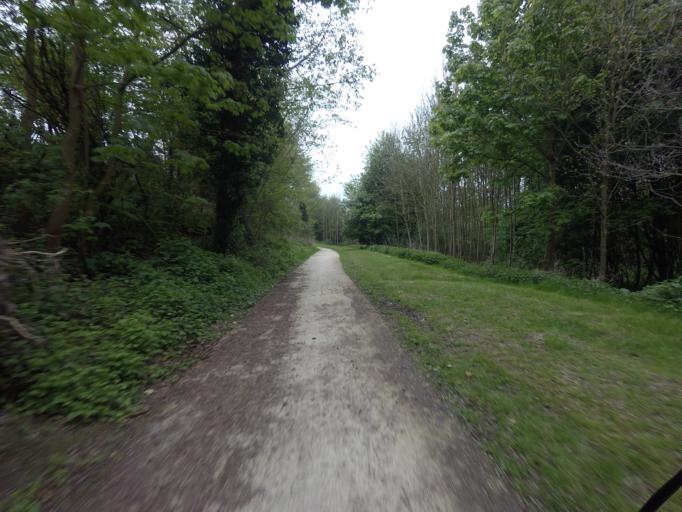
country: BE
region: Flanders
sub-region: Provincie Vlaams-Brabant
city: Vilvoorde
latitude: 50.9236
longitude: 4.4016
